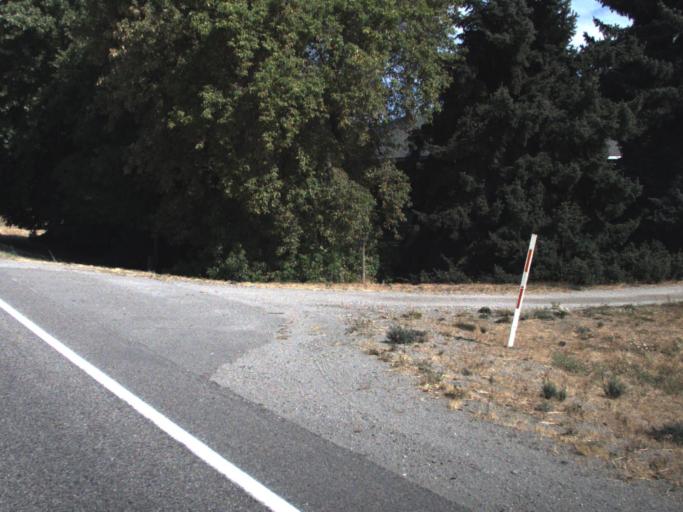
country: US
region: Washington
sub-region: Stevens County
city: Chewelah
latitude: 48.2621
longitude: -117.7153
